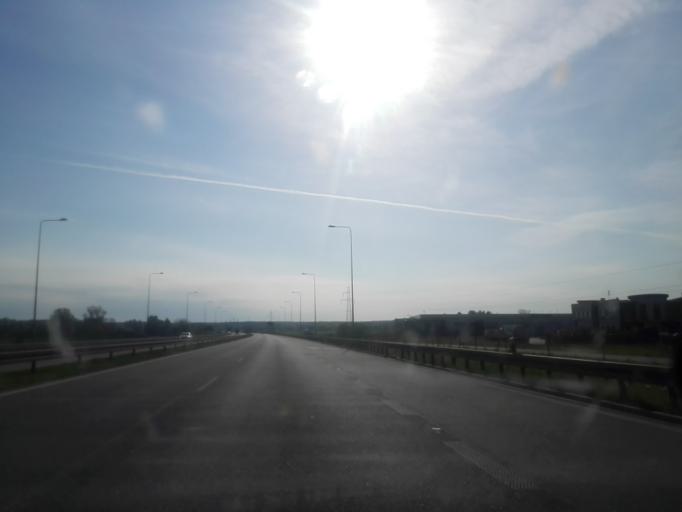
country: PL
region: Lodz Voivodeship
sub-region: Piotrkow Trybunalski
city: Piotrkow Trybunalski
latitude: 51.4435
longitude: 19.7300
